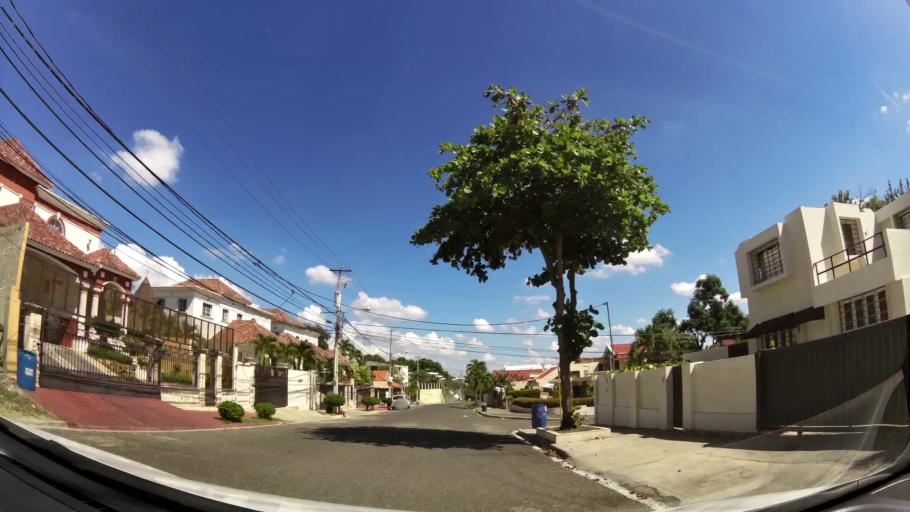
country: DO
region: Santiago
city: Santiago de los Caballeros
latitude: 19.4464
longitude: -70.6935
